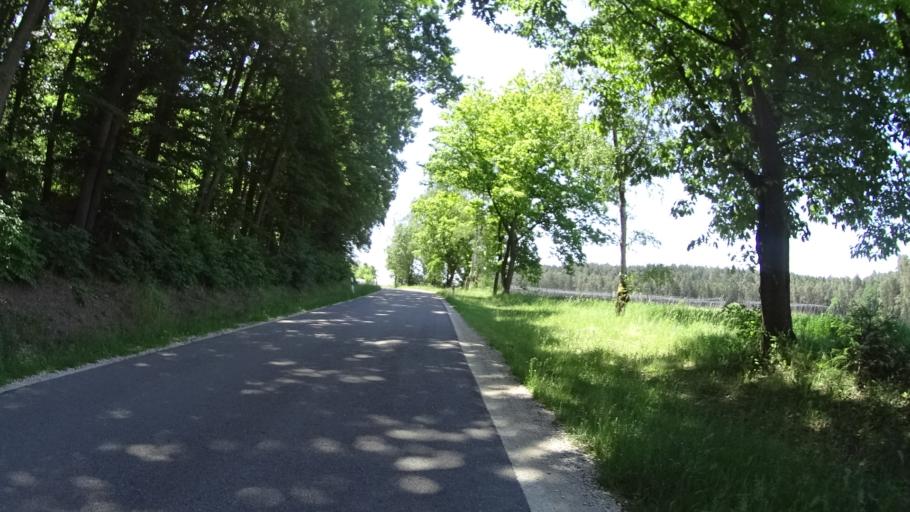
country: DE
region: Bavaria
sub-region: Regierungsbezirk Mittelfranken
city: Pleinfeld
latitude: 49.0904
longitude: 10.9787
